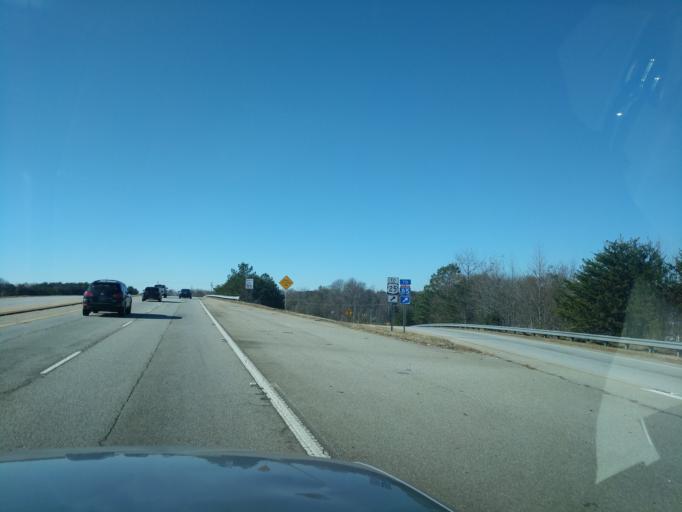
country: US
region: South Carolina
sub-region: Greenville County
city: Welcome
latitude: 34.8348
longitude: -82.4416
